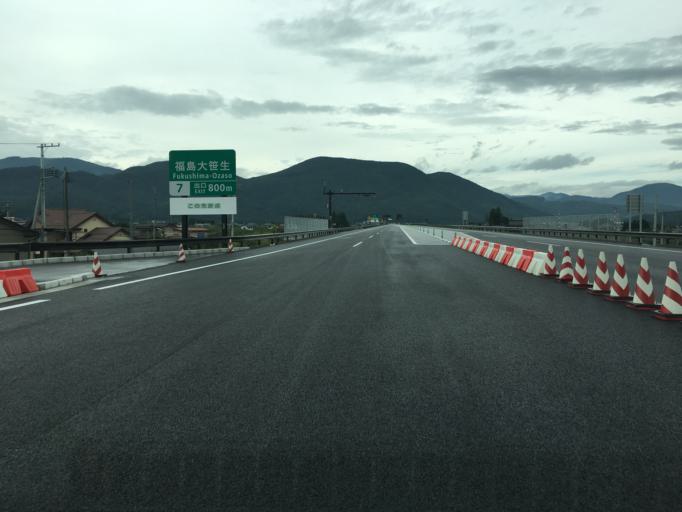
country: JP
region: Fukushima
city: Fukushima-shi
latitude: 37.7924
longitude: 140.4144
